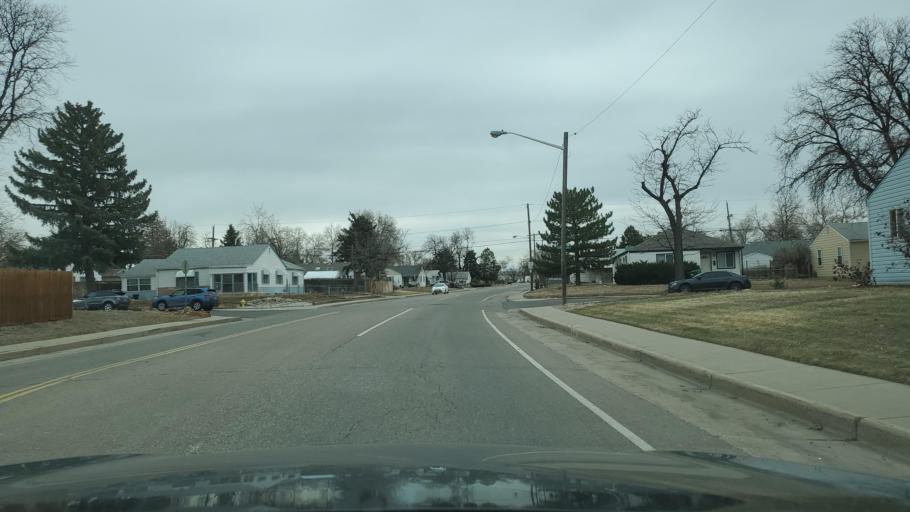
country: US
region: Colorado
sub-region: Adams County
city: Aurora
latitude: 39.7298
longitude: -104.8586
